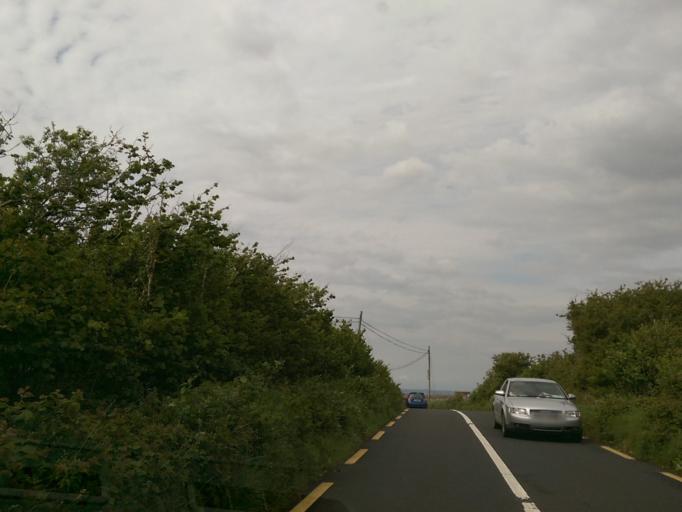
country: IE
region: Connaught
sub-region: County Galway
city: Bearna
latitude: 53.0677
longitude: -9.1840
